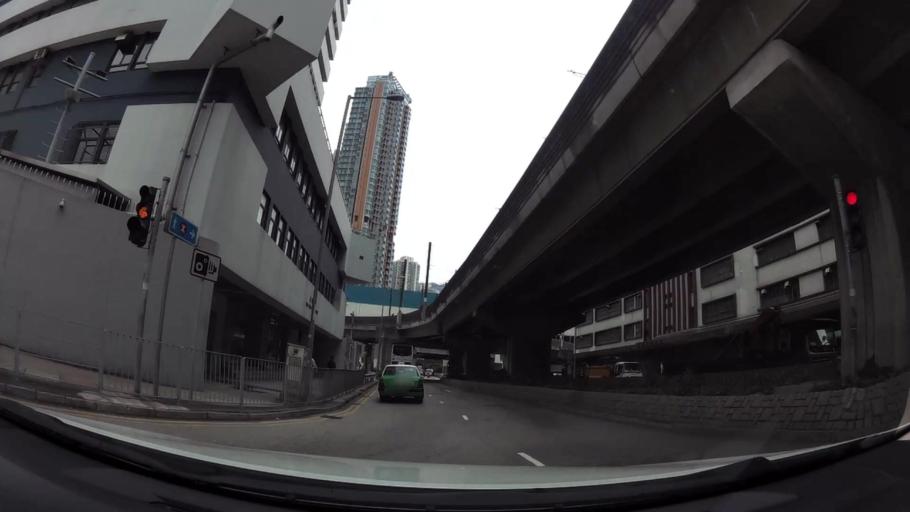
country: HK
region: Tuen Mun
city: Tuen Mun
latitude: 22.3947
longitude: 113.9715
